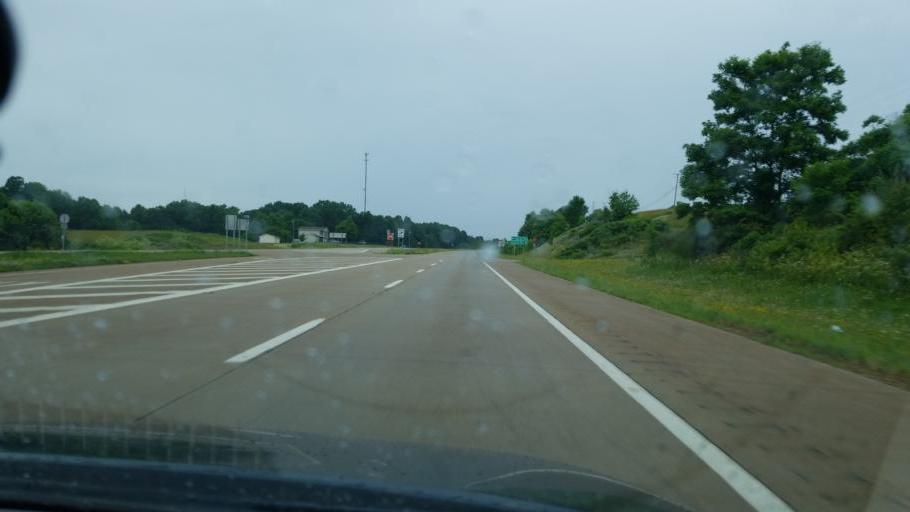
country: US
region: West Virginia
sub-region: Wood County
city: Washington
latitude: 39.2300
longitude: -81.8784
